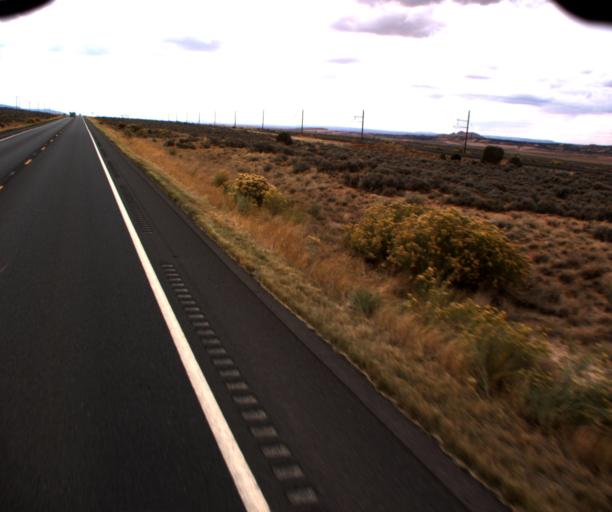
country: US
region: Arizona
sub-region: Navajo County
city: Kayenta
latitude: 36.5329
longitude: -110.5636
